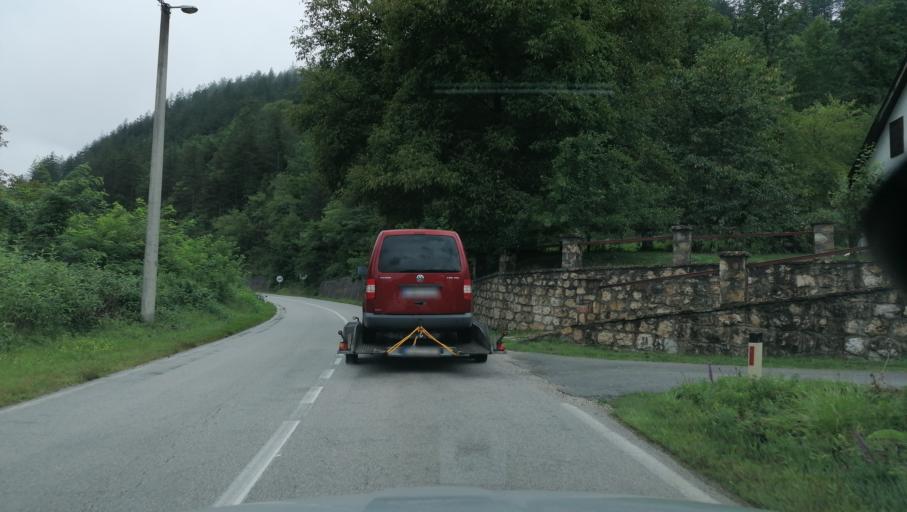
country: BA
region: Republika Srpska
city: Visegrad
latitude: 43.7828
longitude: 19.3553
